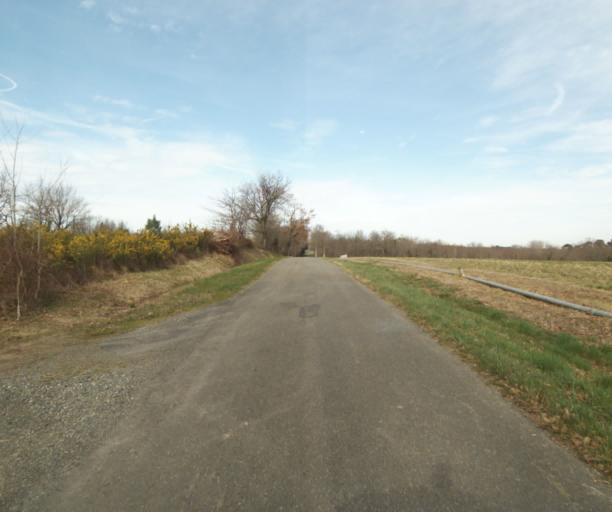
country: FR
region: Midi-Pyrenees
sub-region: Departement du Gers
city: Eauze
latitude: 43.9057
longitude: 0.0357
